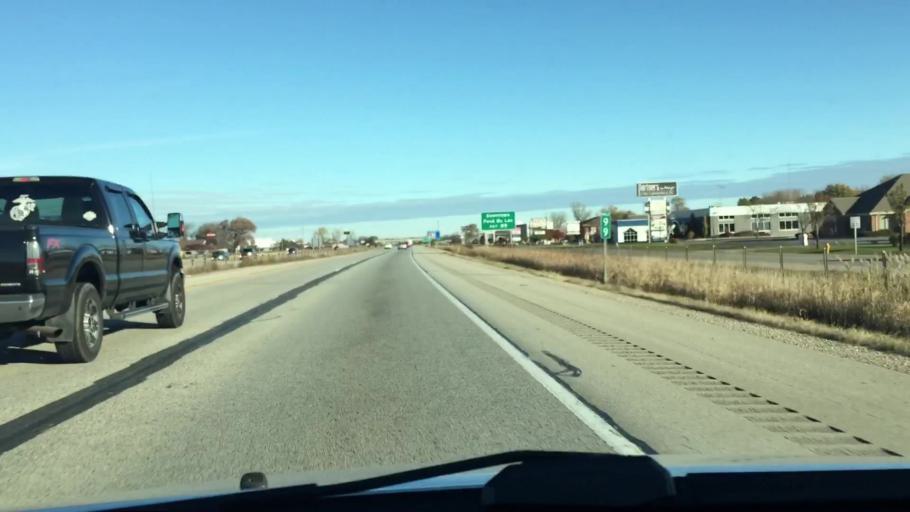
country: US
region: Wisconsin
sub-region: Fond du Lac County
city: North Fond du Lac
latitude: 43.7733
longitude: -88.4821
